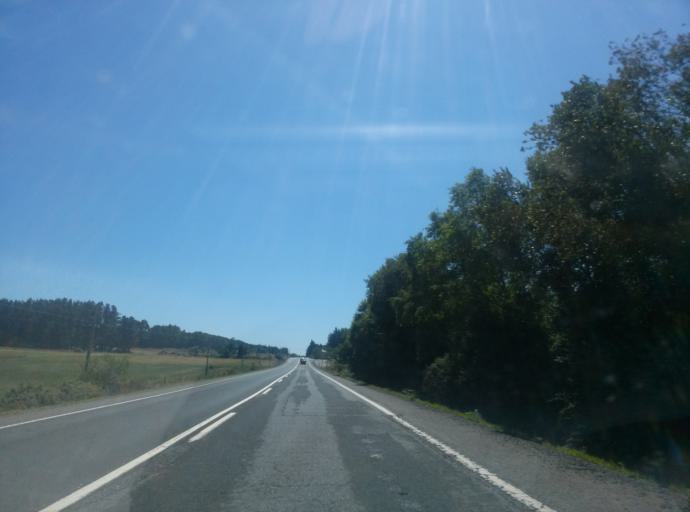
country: ES
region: Galicia
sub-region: Provincia de Lugo
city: Castro de Rei
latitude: 43.1300
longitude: -7.4179
